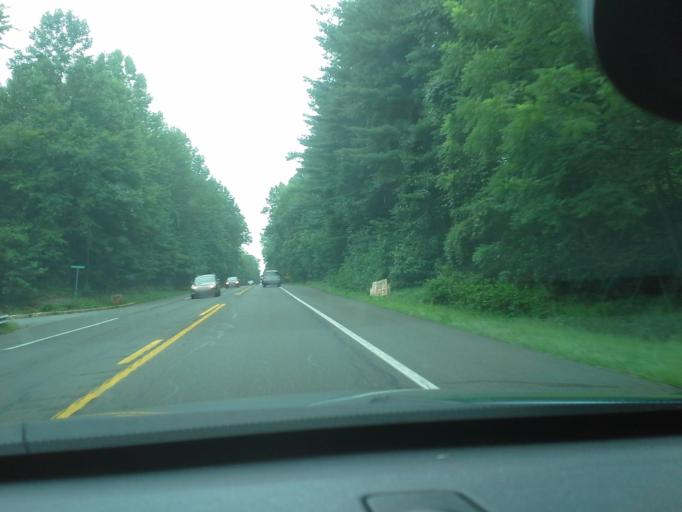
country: US
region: Maryland
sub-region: Calvert County
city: Dunkirk Town Center
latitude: 38.7403
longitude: -76.6293
